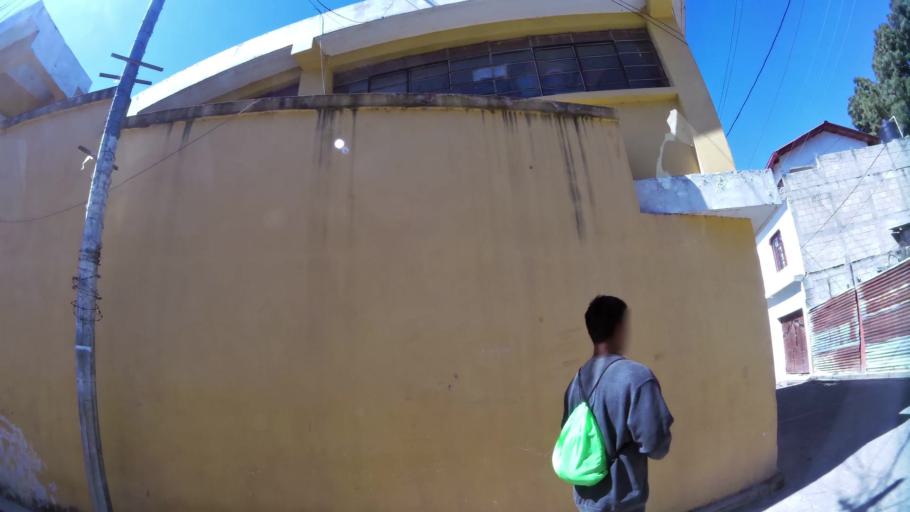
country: GT
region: Solola
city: Panajachel
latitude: 14.7382
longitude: -91.1526
